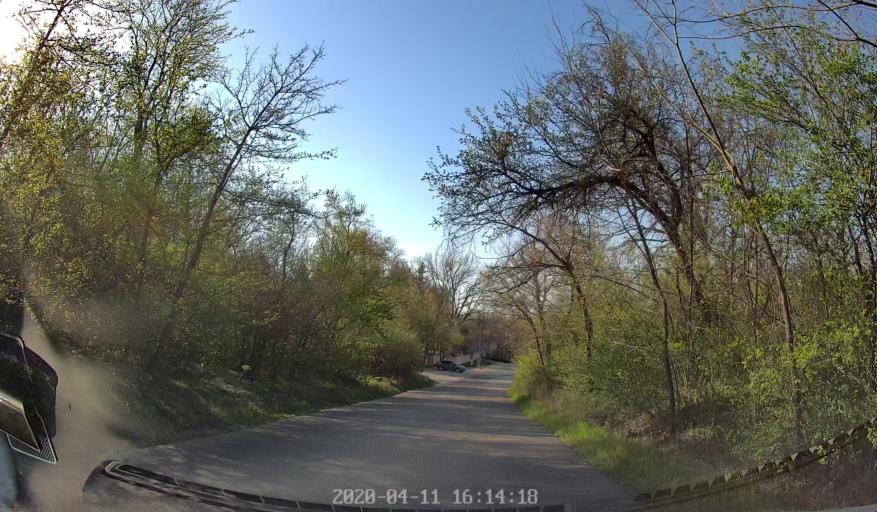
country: MD
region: Chisinau
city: Vadul lui Voda
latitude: 47.0745
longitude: 29.1016
